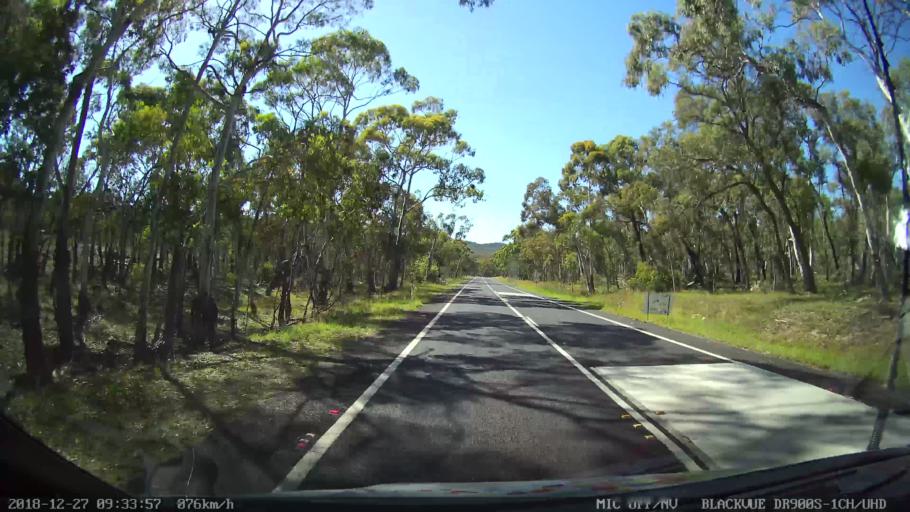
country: AU
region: New South Wales
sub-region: Lithgow
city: Portland
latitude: -33.2208
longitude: 150.0246
